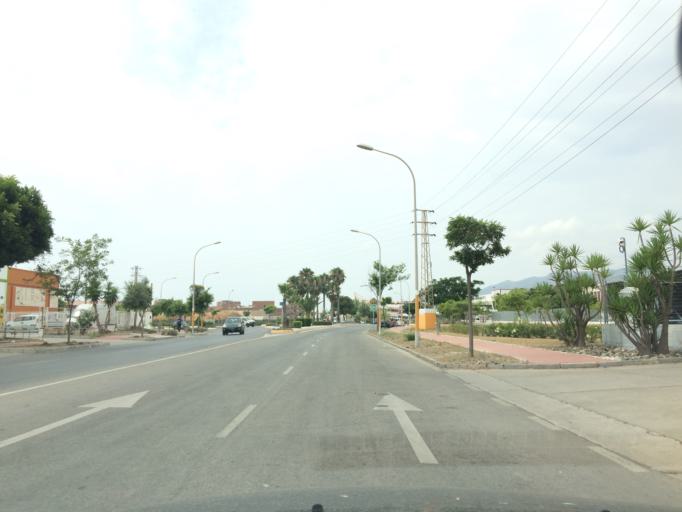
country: ES
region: Andalusia
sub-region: Provincia de Malaga
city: Malaga
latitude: 36.6958
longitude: -4.4841
